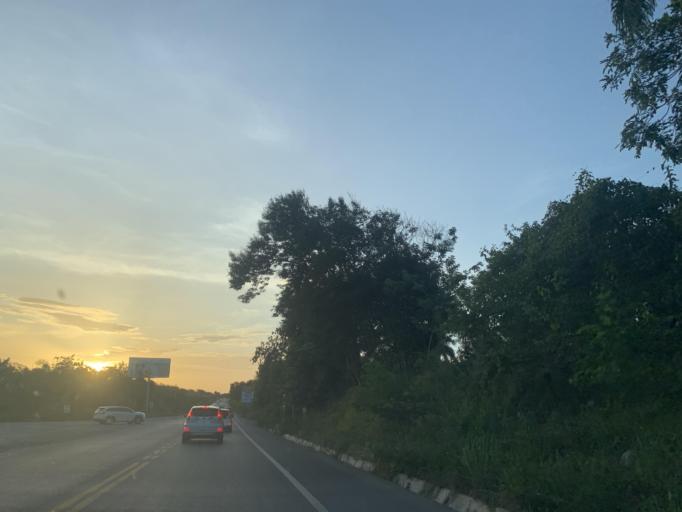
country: DO
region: Puerto Plata
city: Imbert
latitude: 19.7700
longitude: -70.8390
